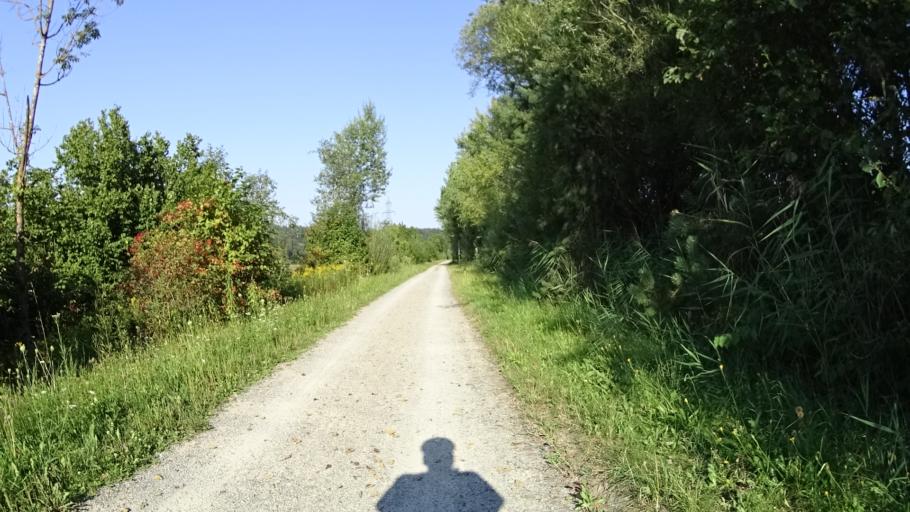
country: AT
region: Carinthia
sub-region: Politischer Bezirk Villach Land
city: Wernberg
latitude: 46.5944
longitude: 13.9707
